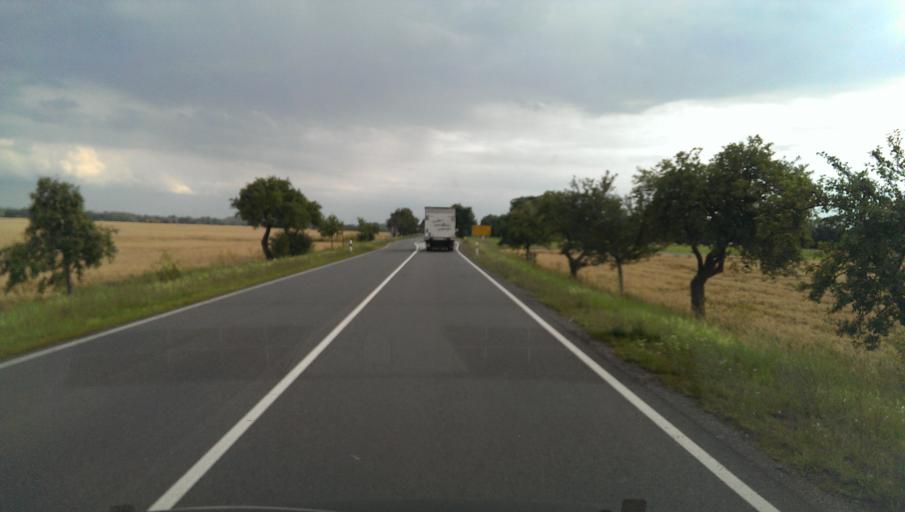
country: DE
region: Saxony
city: Pegau
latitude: 51.1535
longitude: 12.2480
